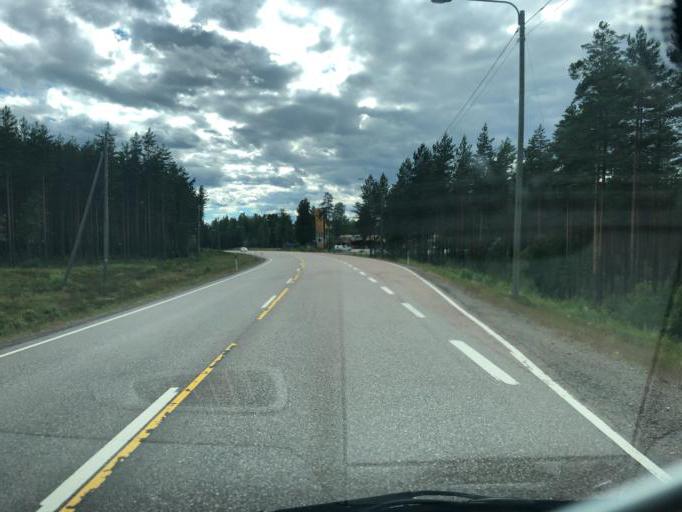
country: FI
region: Southern Savonia
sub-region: Mikkeli
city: Maentyharju
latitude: 61.0927
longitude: 27.0718
